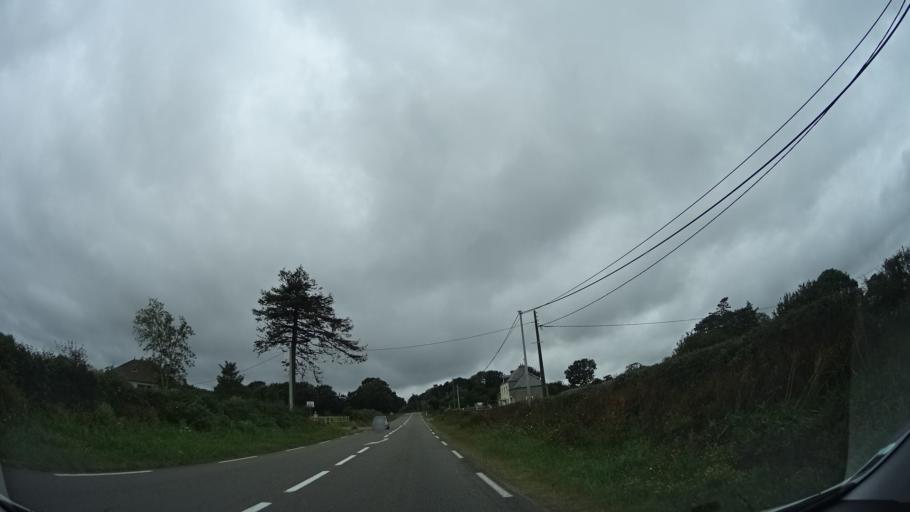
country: FR
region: Lower Normandy
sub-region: Departement de la Manche
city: La Haye-du-Puits
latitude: 49.3026
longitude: -1.5814
